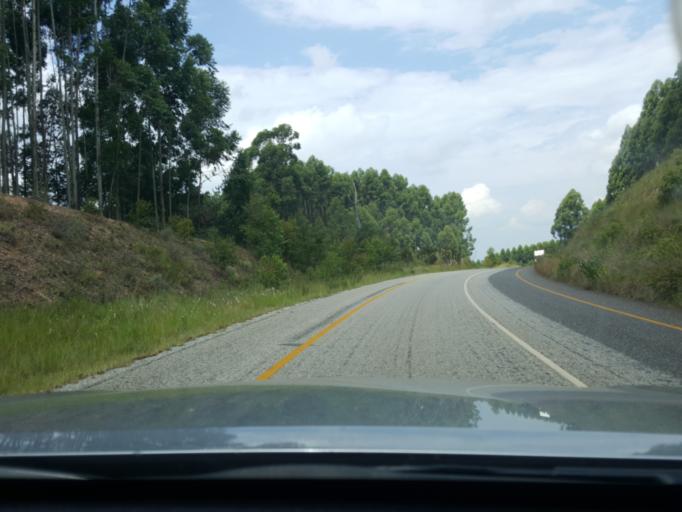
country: ZA
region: Mpumalanga
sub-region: Ehlanzeni District
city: White River
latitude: -25.1858
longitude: 30.8942
